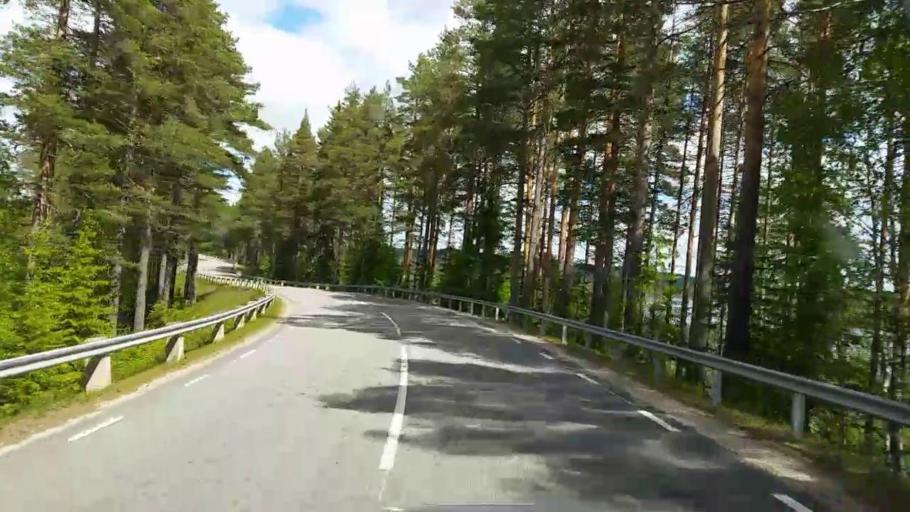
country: SE
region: Gaevleborg
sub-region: Bollnas Kommun
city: Vittsjo
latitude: 61.1229
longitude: 16.1735
